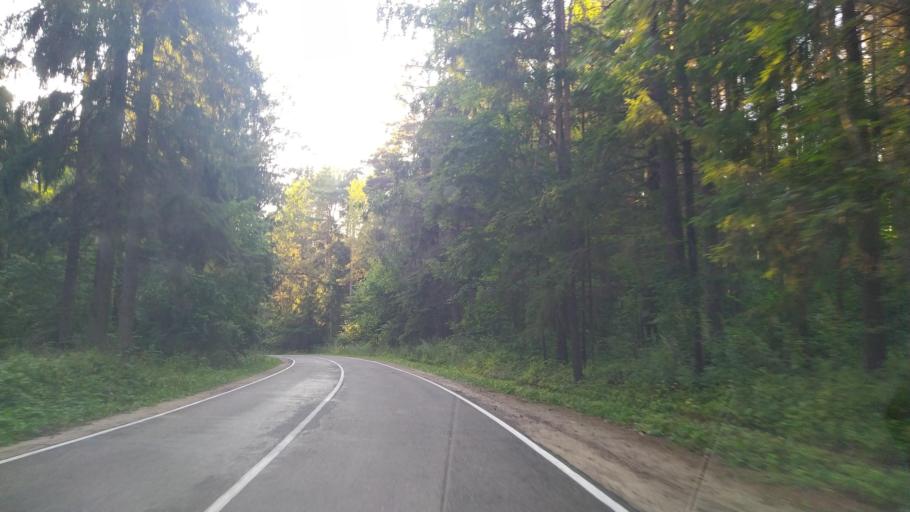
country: RU
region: Pskov
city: Pushkinskiye Gory
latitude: 57.0340
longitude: 28.9187
